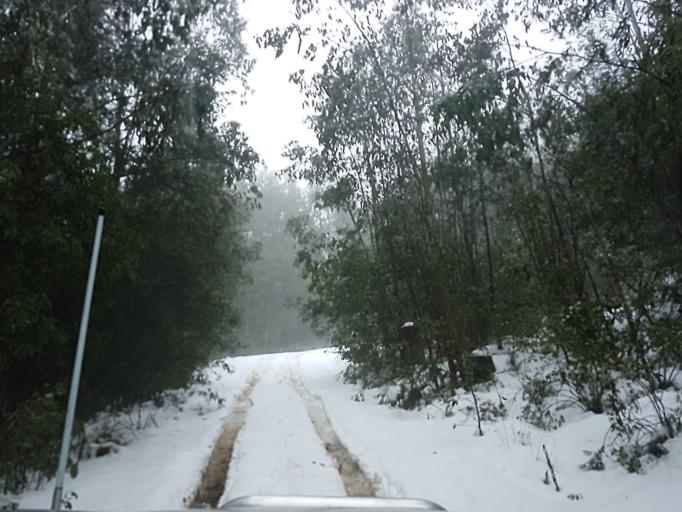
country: AU
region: Victoria
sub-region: Yarra Ranges
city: Millgrove
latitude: -37.5369
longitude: 145.8943
